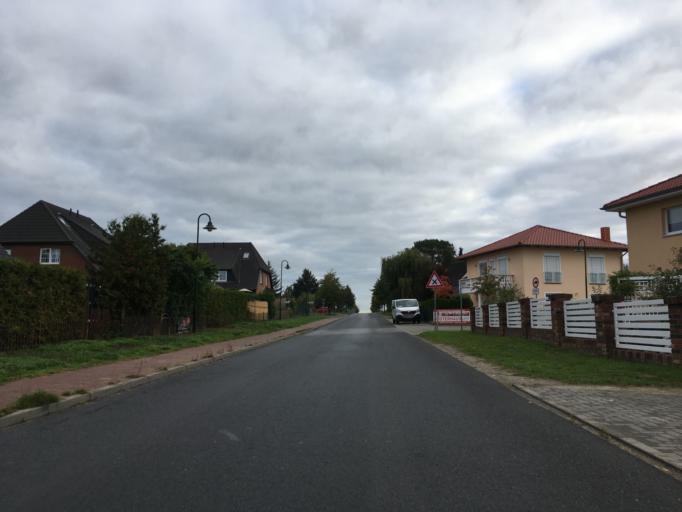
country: DE
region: Berlin
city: Falkenberg
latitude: 52.5979
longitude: 13.5536
